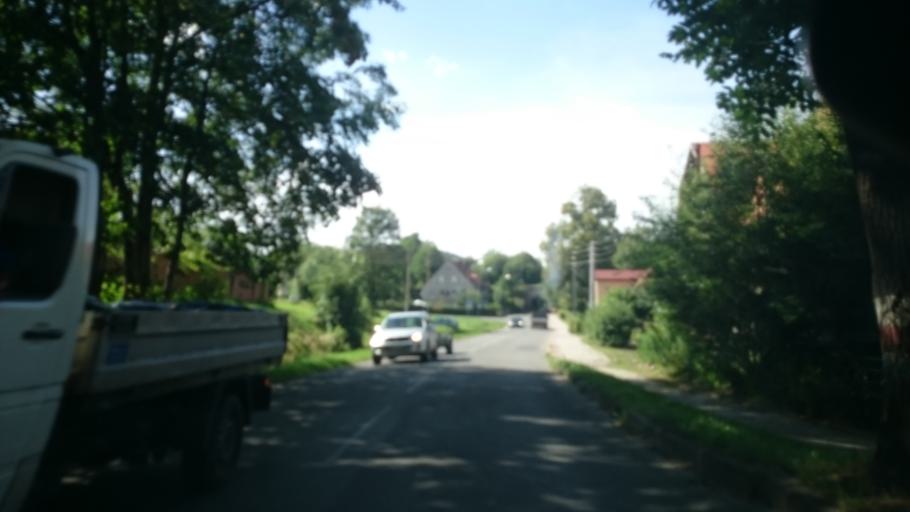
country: PL
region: Lower Silesian Voivodeship
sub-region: Powiat klodzki
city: Polanica-Zdroj
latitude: 50.3966
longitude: 16.5193
